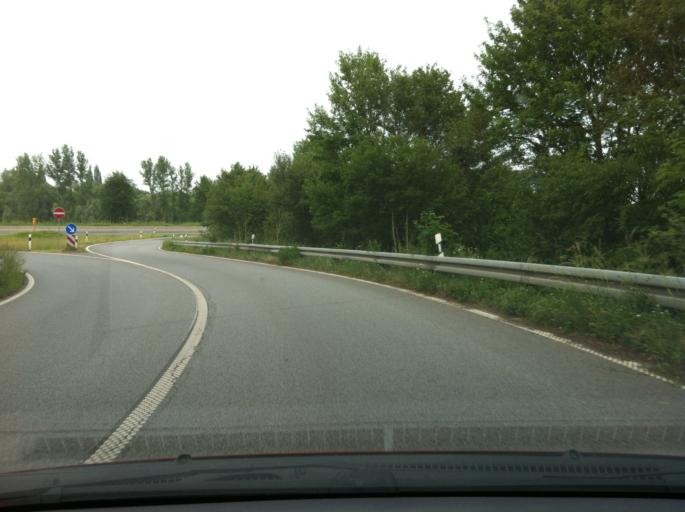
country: DE
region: Hesse
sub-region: Regierungsbezirk Darmstadt
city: Gross-Zimmern
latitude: 49.8859
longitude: 8.8336
